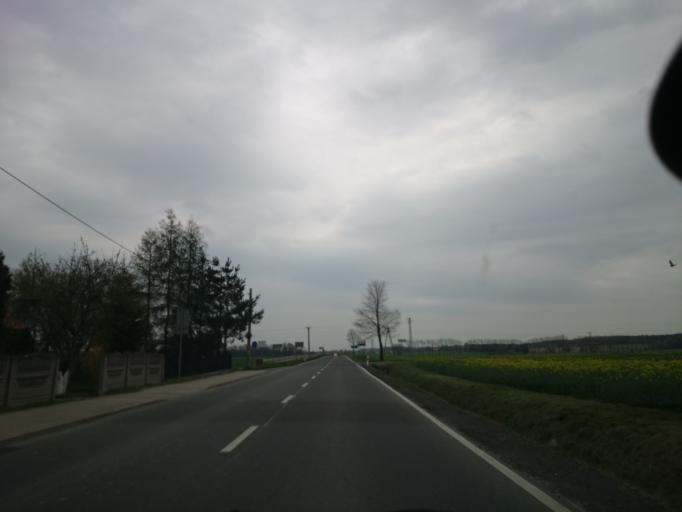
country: PL
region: Opole Voivodeship
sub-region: Powiat nyski
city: Glucholazy
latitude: 50.3176
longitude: 17.4072
